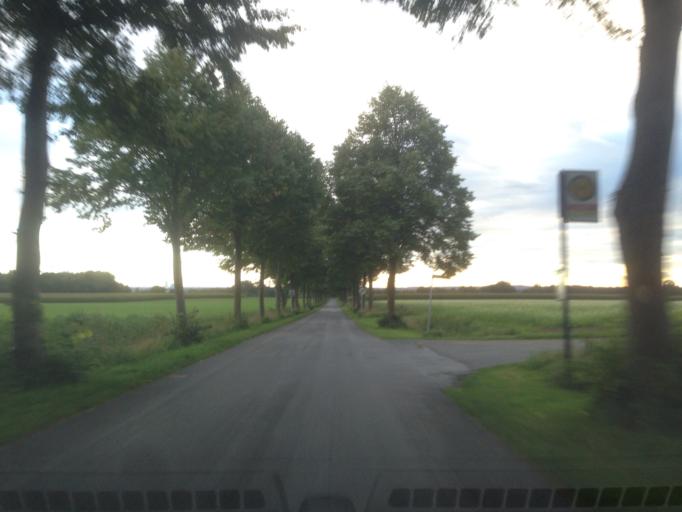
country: DE
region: North Rhine-Westphalia
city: Olfen
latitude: 51.7477
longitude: 7.3893
